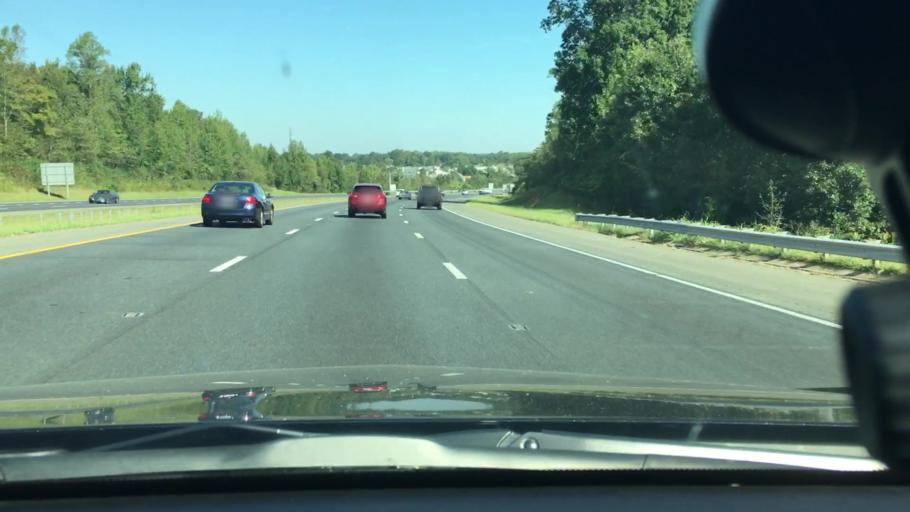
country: US
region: North Carolina
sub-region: Mecklenburg County
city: Mint Hill
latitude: 35.2285
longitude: -80.6541
